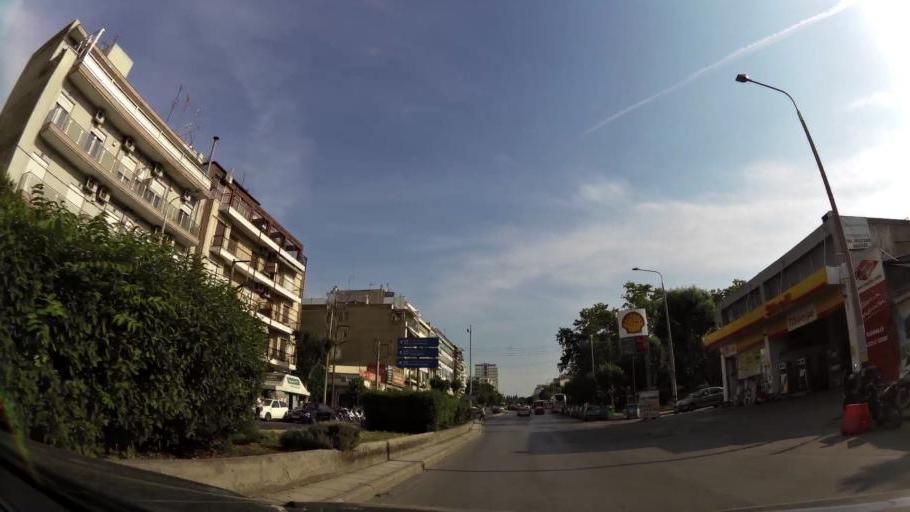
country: GR
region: Central Macedonia
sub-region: Nomos Thessalonikis
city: Thessaloniki
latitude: 40.6434
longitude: 22.9353
